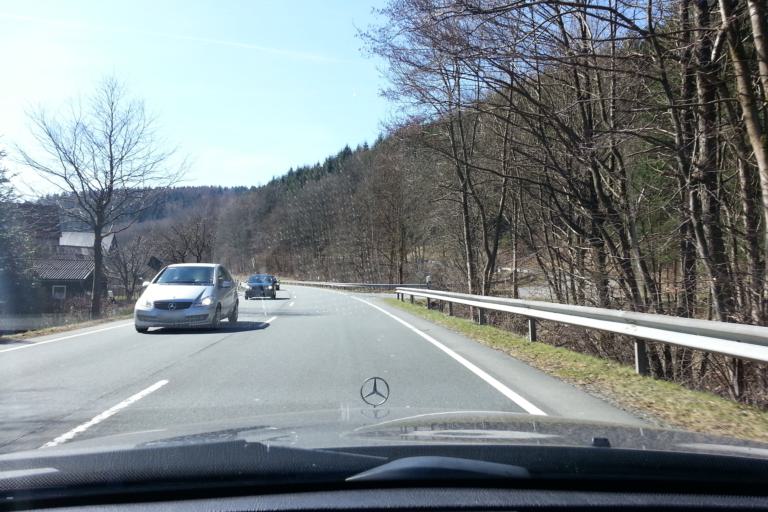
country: DE
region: North Rhine-Westphalia
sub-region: Regierungsbezirk Arnsberg
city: Bad Fredeburg
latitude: 51.2464
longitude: 8.3588
